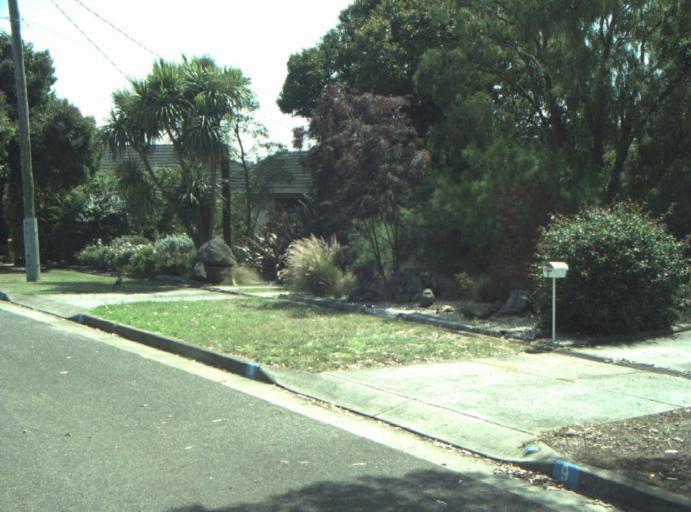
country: AU
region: Victoria
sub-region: Greater Geelong
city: Wandana Heights
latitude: -38.1694
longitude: 144.3230
